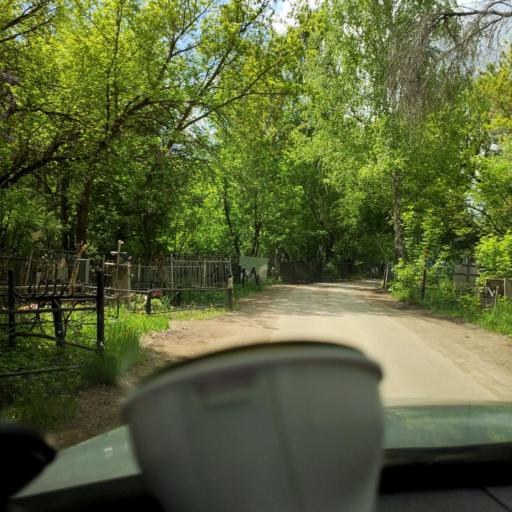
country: RU
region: Samara
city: Petra-Dubrava
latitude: 53.2748
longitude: 50.3223
